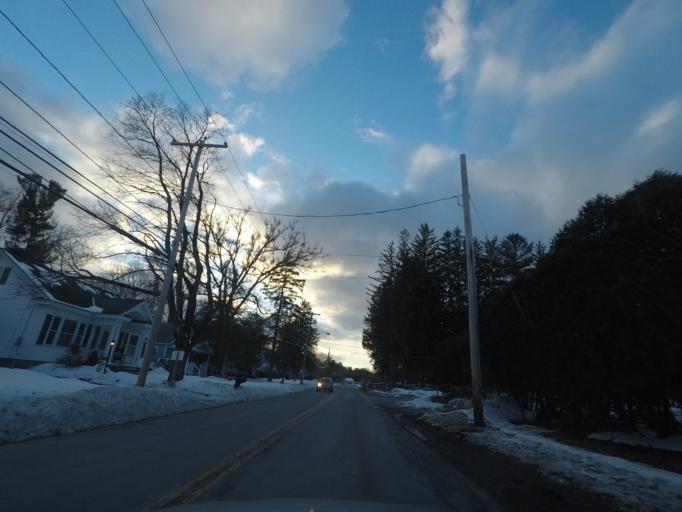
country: US
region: New York
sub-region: Schenectady County
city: Scotia
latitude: 42.8494
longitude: -73.9456
